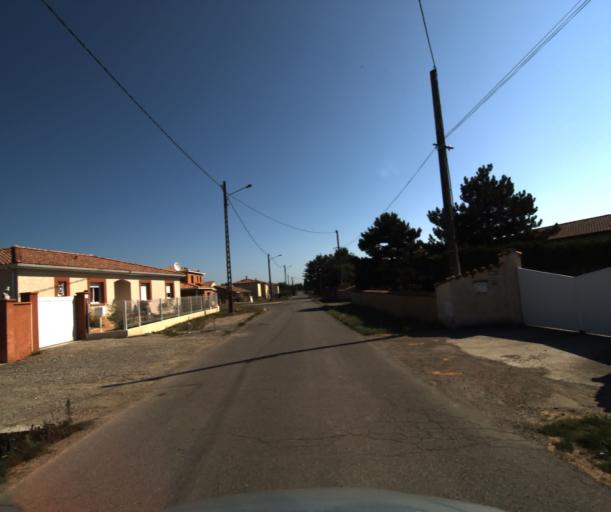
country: FR
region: Midi-Pyrenees
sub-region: Departement de la Haute-Garonne
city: Eaunes
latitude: 43.4324
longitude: 1.3628
